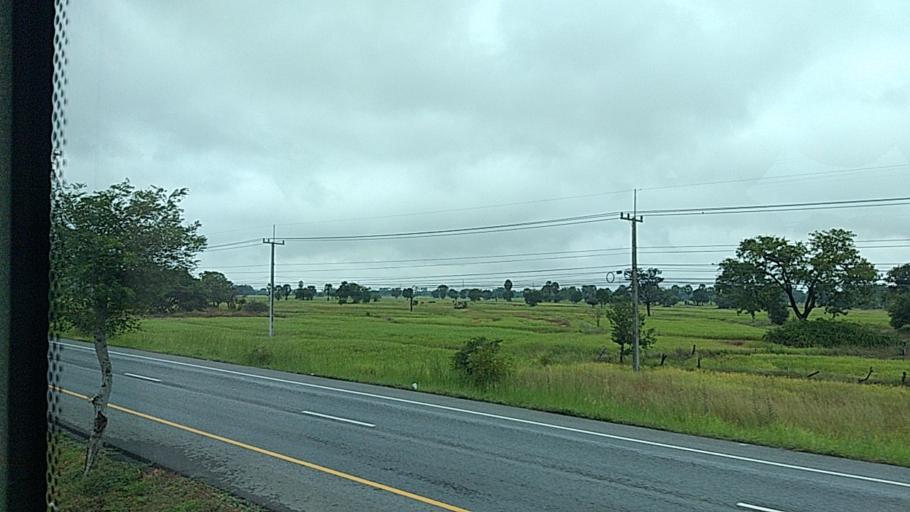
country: TH
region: Nakhon Ratchasima
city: Non Daeng
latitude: 15.4208
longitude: 102.4837
